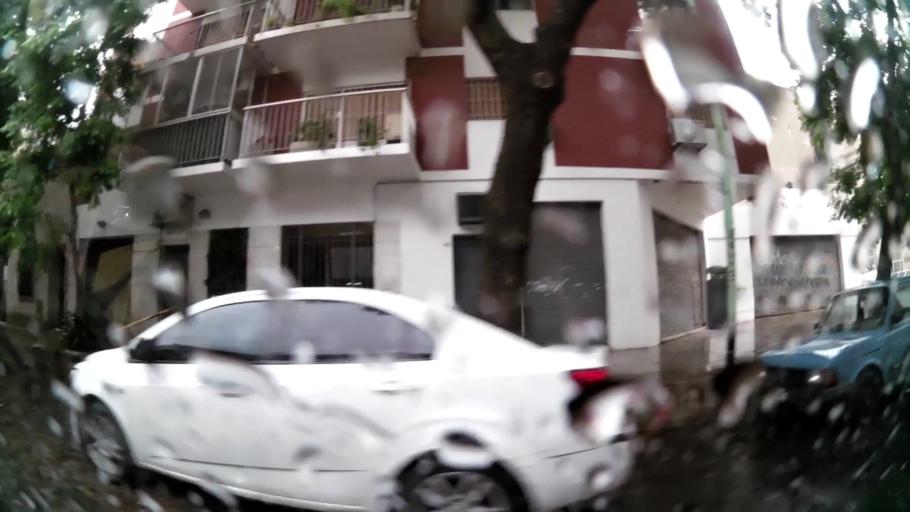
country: AR
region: Buenos Aires
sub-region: Partido de Avellaneda
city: Avellaneda
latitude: -34.6381
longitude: -58.3704
